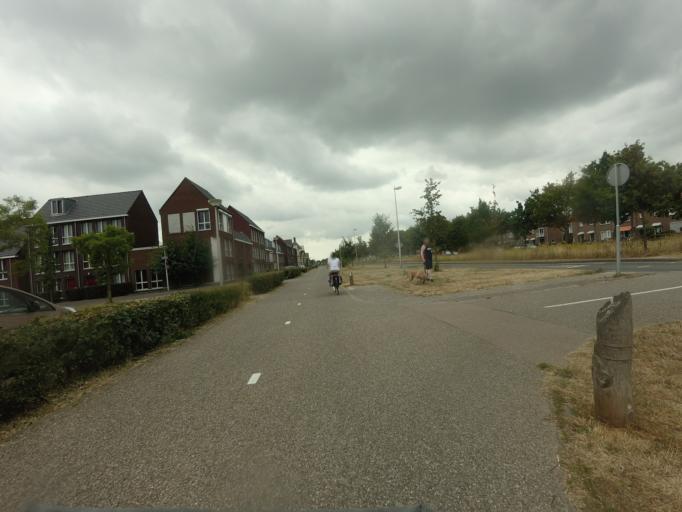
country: NL
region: Utrecht
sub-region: Stichtse Vecht
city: Spechtenkamp
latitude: 52.0992
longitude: 5.0110
